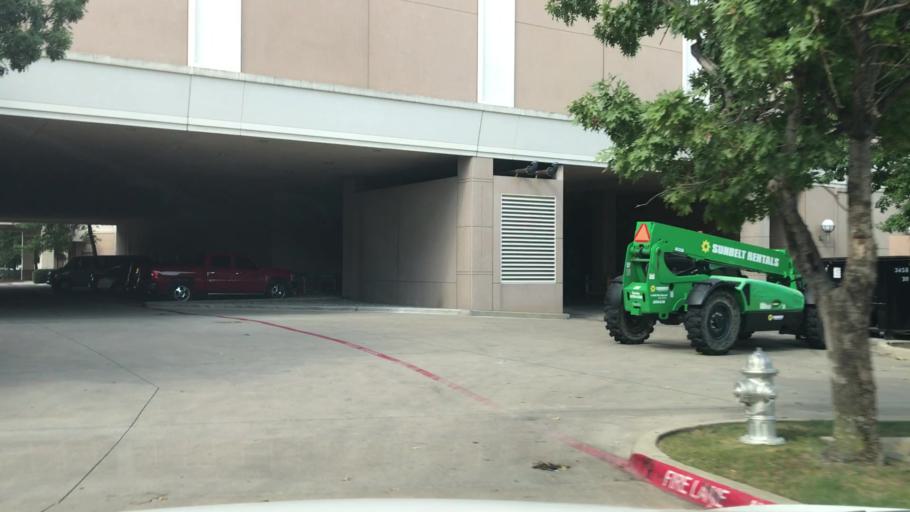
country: US
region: Texas
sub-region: Dallas County
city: Irving
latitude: 32.8717
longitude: -96.9420
